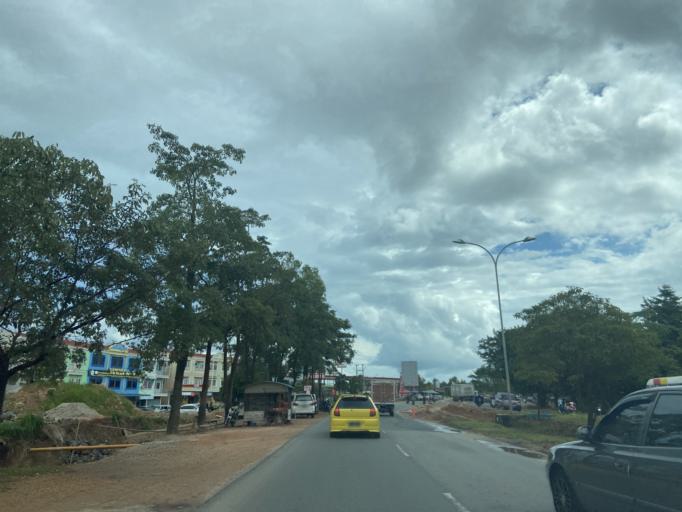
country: SG
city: Singapore
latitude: 1.0407
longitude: 103.9874
